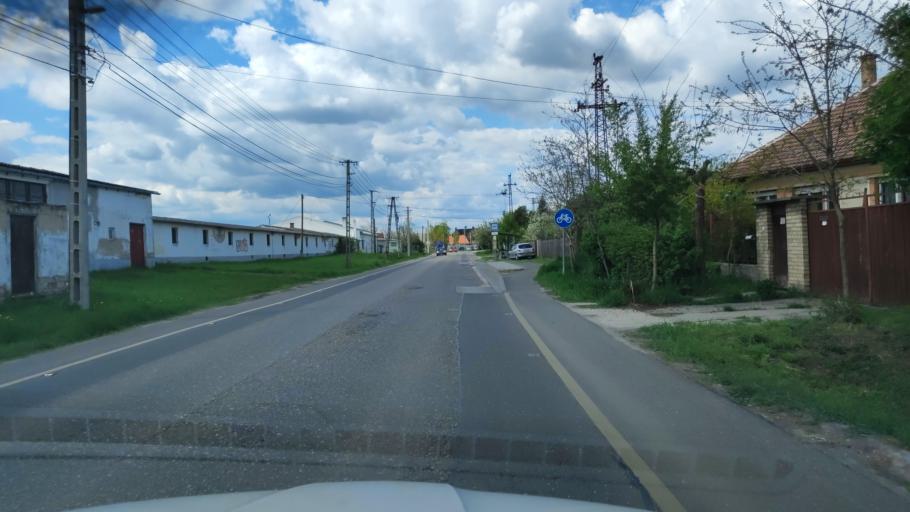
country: HU
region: Pest
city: Cegled
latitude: 47.1856
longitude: 19.7805
